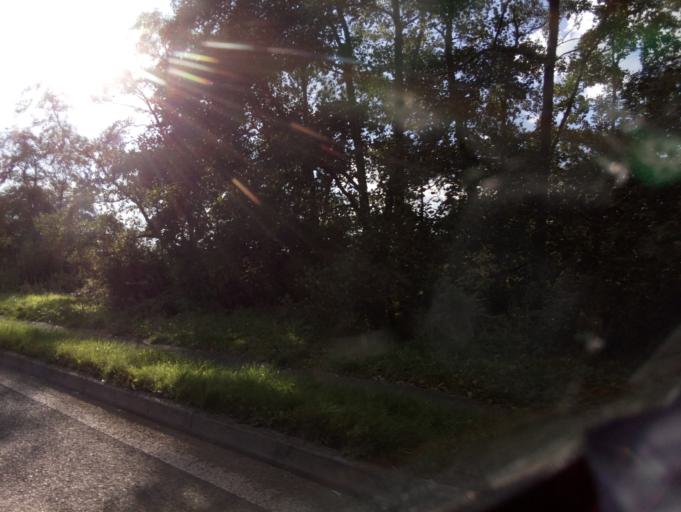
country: GB
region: Wales
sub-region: Sir Powys
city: Hay
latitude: 52.0406
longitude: -3.2009
